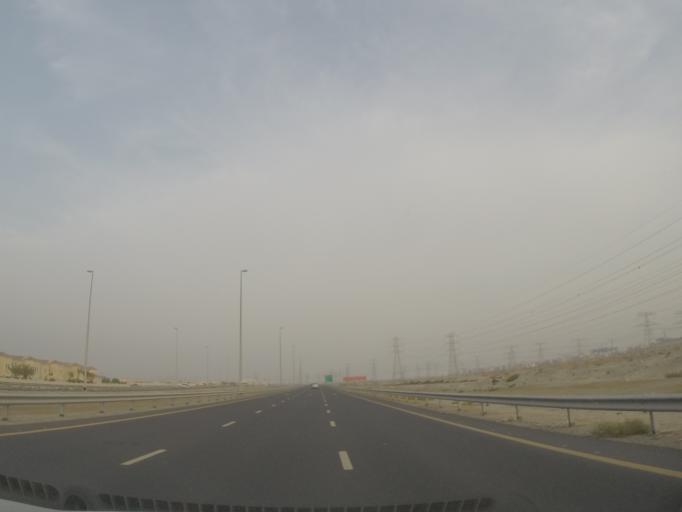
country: AE
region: Dubai
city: Dubai
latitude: 25.0434
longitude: 55.1525
